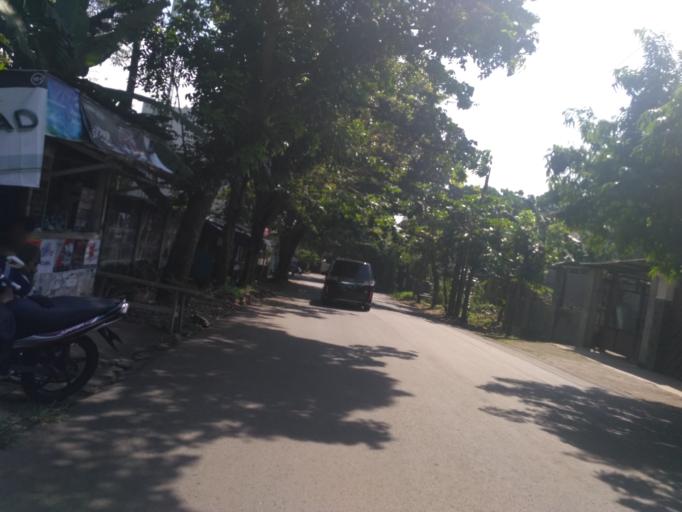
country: ID
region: Central Java
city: Semarang
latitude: -7.0252
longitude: 110.4136
